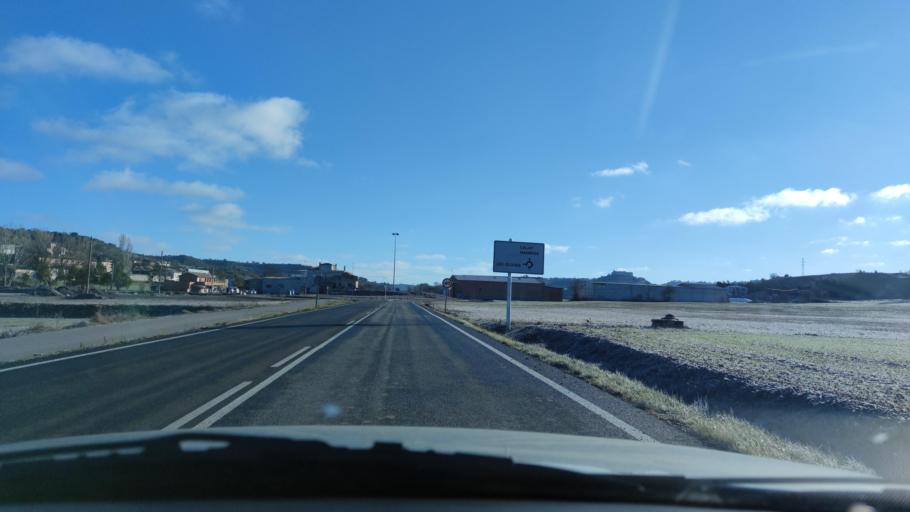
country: ES
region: Catalonia
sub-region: Provincia de Lleida
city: Cervera
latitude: 41.6942
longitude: 1.3178
